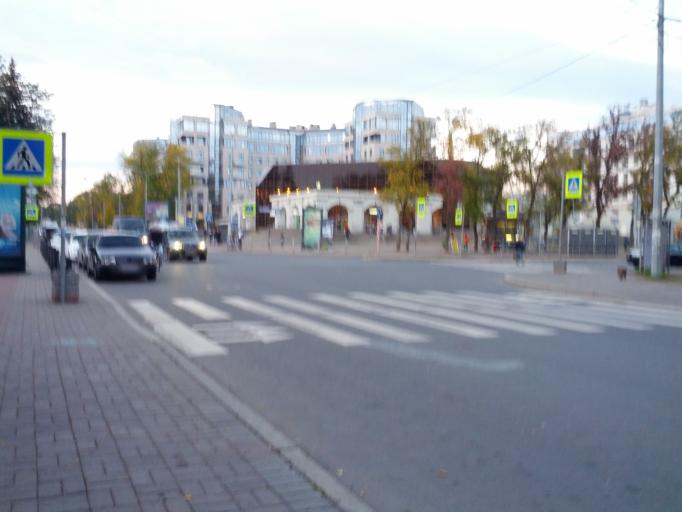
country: RU
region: Leningrad
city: Krestovskiy ostrov
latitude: 59.9709
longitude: 30.2588
